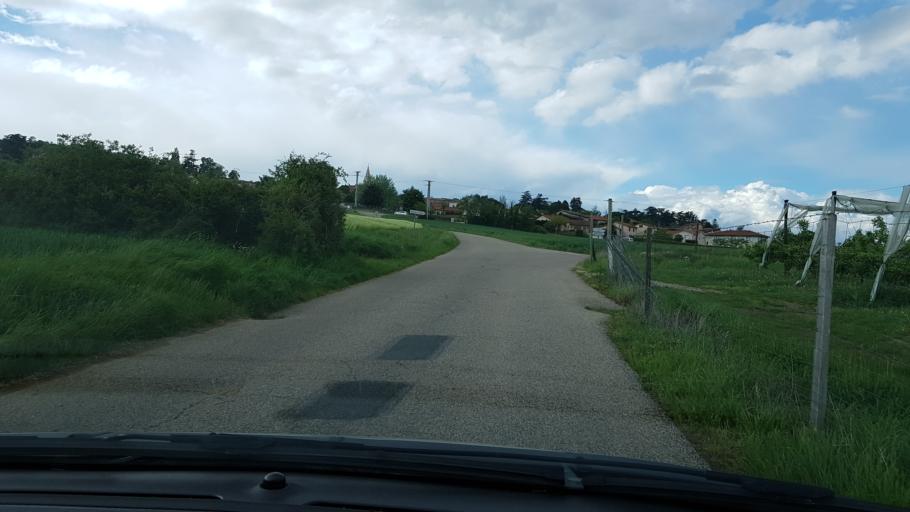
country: FR
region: Rhone-Alpes
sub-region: Departement du Rhone
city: Saint-Maurice-sur-Dargoire
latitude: 45.5783
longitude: 4.6366
